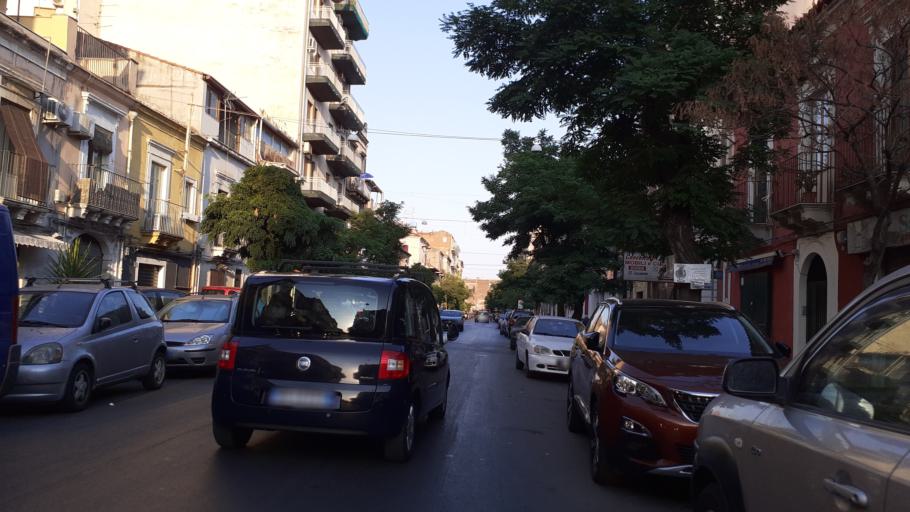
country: IT
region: Sicily
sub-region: Catania
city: Catania
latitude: 37.4984
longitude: 15.0811
